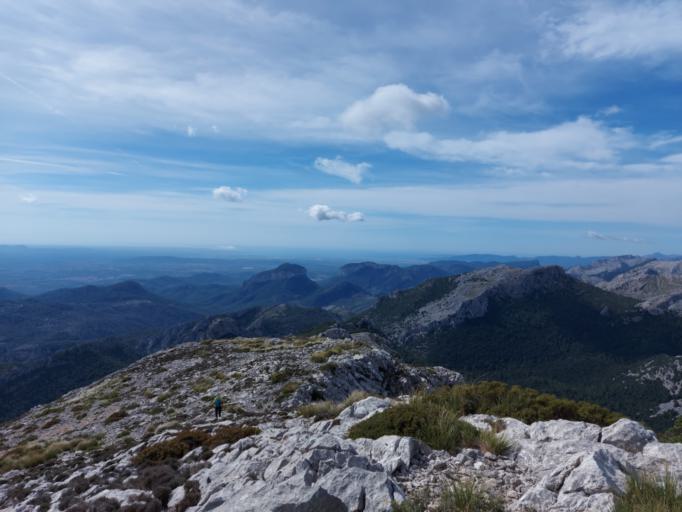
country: ES
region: Balearic Islands
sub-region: Illes Balears
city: Escorca
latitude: 39.7990
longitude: 2.8435
